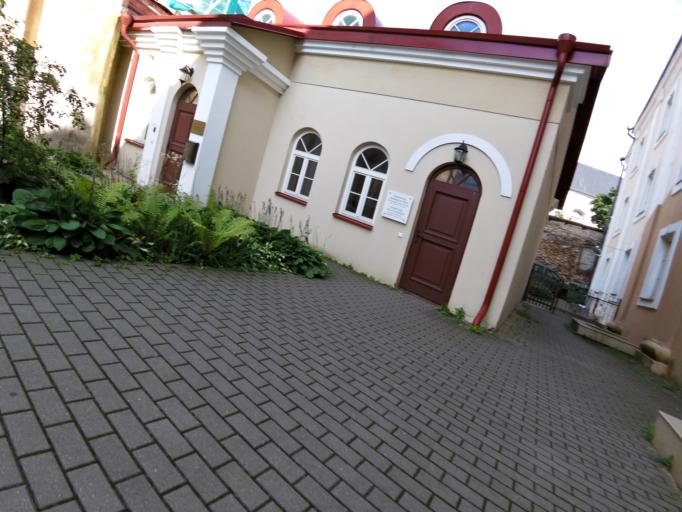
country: LT
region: Vilnius County
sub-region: Vilnius
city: Vilnius
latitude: 54.6750
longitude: 25.2883
